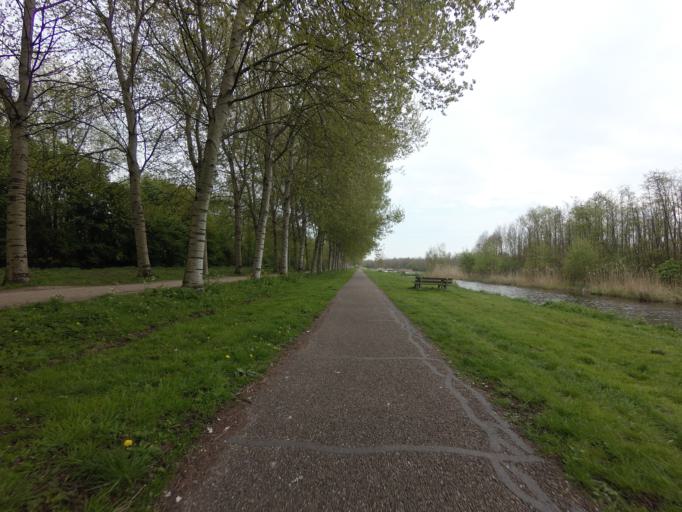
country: NL
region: North Holland
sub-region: Gemeente Diemen
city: Diemen
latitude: 52.3319
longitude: 4.9907
